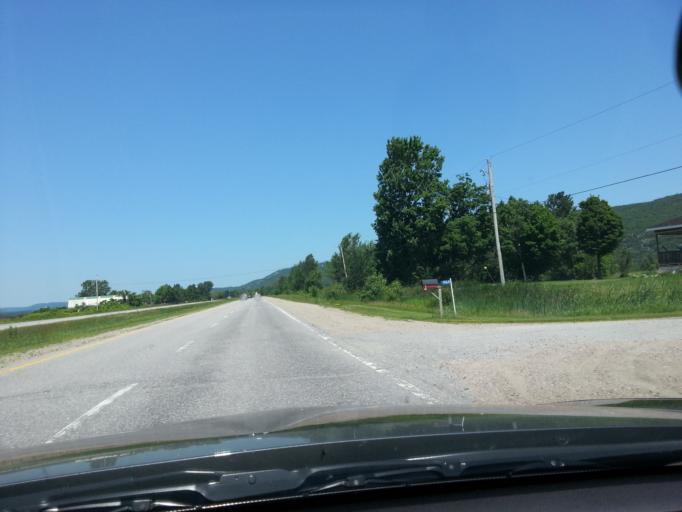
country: CA
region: Quebec
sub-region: Outaouais
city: Wakefield
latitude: 45.5187
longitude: -75.9858
